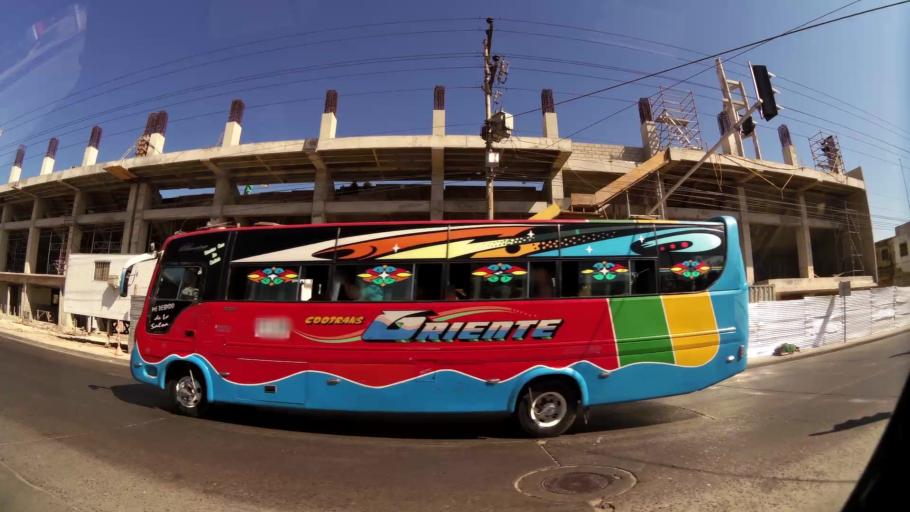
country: CO
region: Atlantico
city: Barranquilla
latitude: 10.9643
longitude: -74.7826
